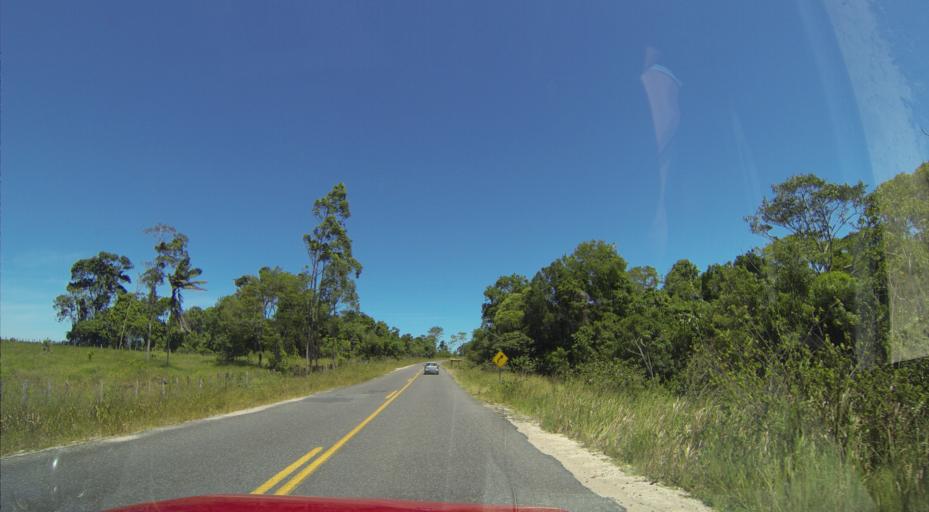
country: BR
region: Bahia
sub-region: Prado
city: Prado
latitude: -17.2757
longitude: -39.3303
